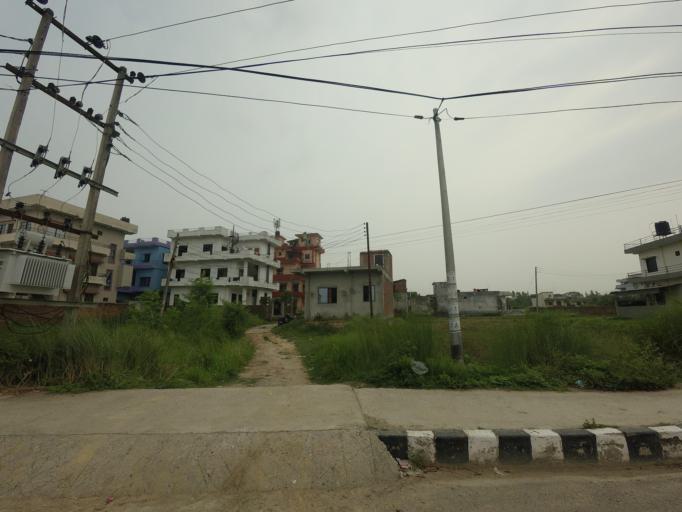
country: NP
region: Western Region
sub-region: Lumbini Zone
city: Bhairahawa
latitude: 27.4929
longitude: 83.4572
